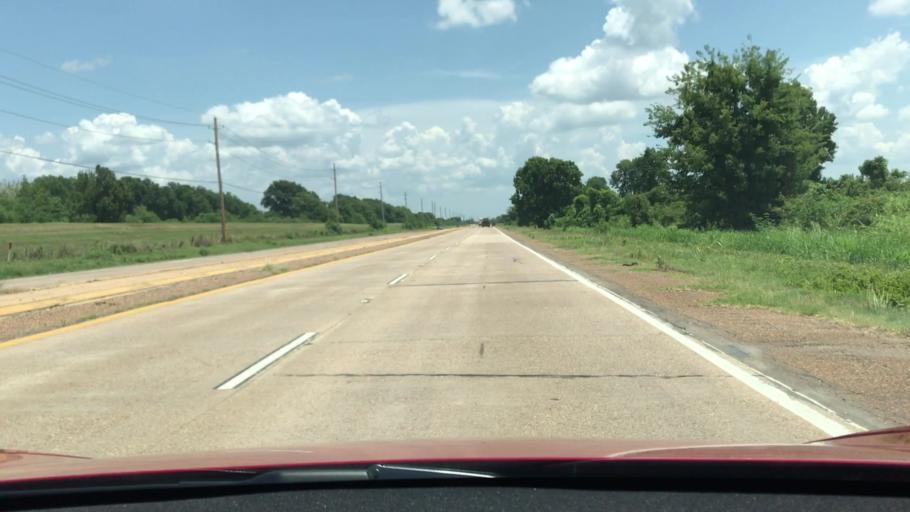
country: US
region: Louisiana
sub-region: Bossier Parish
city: Bossier City
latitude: 32.3878
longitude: -93.6795
